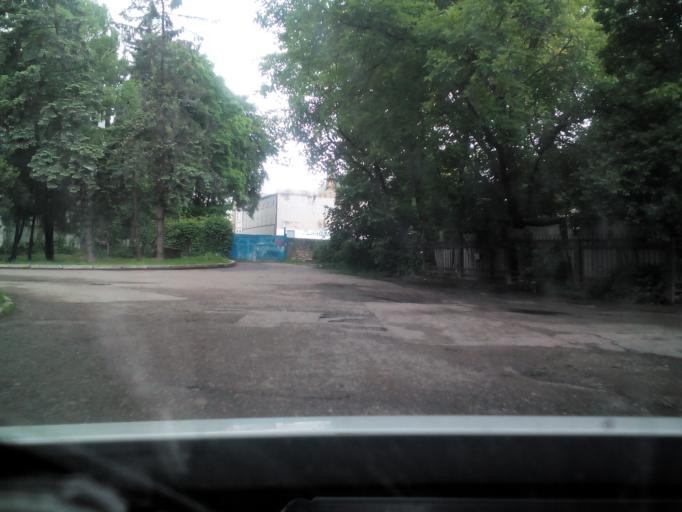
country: RU
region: Stavropol'skiy
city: Svobody
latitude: 44.0348
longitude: 43.0600
